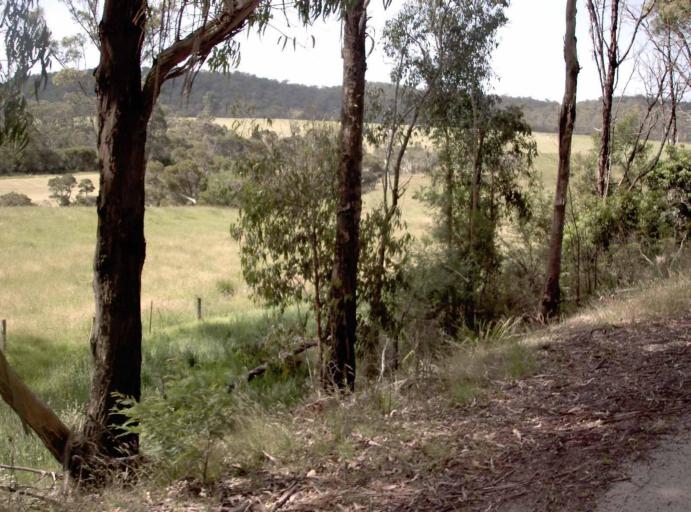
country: AU
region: New South Wales
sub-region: Bega Valley
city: Eden
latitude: -37.4809
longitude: 149.6315
